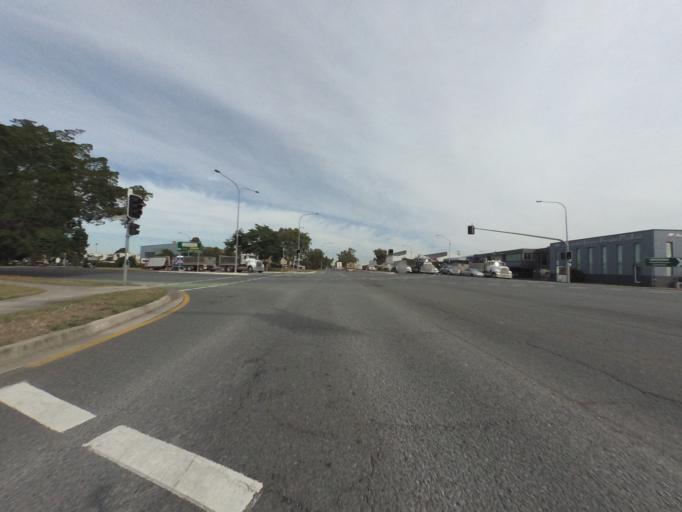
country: AU
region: Queensland
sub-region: Brisbane
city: Ascot
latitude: -27.4316
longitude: 153.0886
